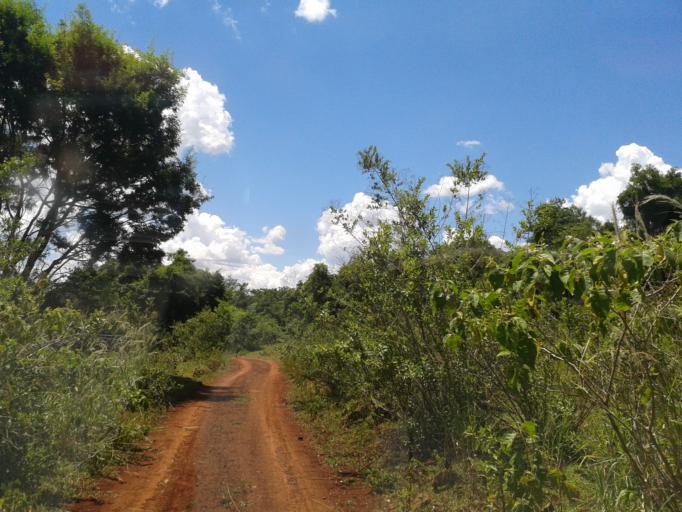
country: BR
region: Minas Gerais
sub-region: Centralina
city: Centralina
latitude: -18.6884
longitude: -49.1791
